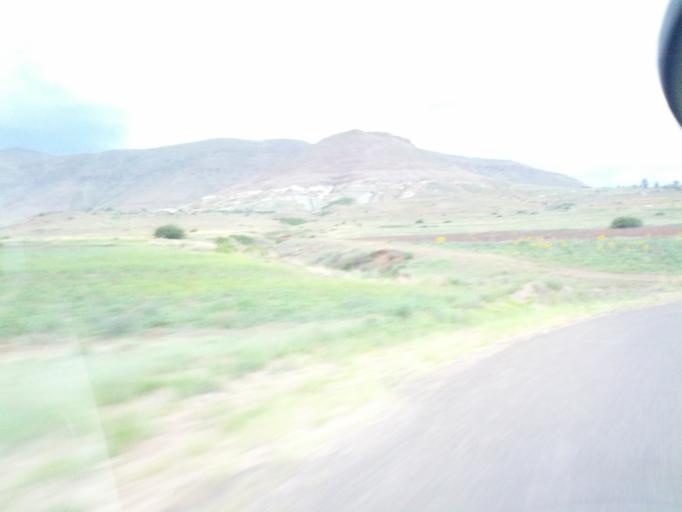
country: LS
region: Qacha's Nek
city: Qacha's Nek
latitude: -30.0543
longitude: 28.3781
